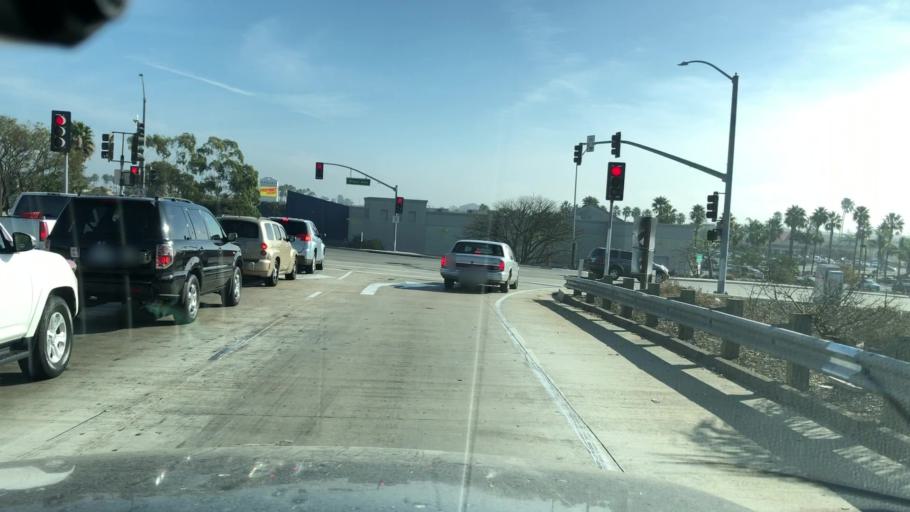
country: US
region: California
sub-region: Ventura County
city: El Rio
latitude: 34.2240
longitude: -119.1592
